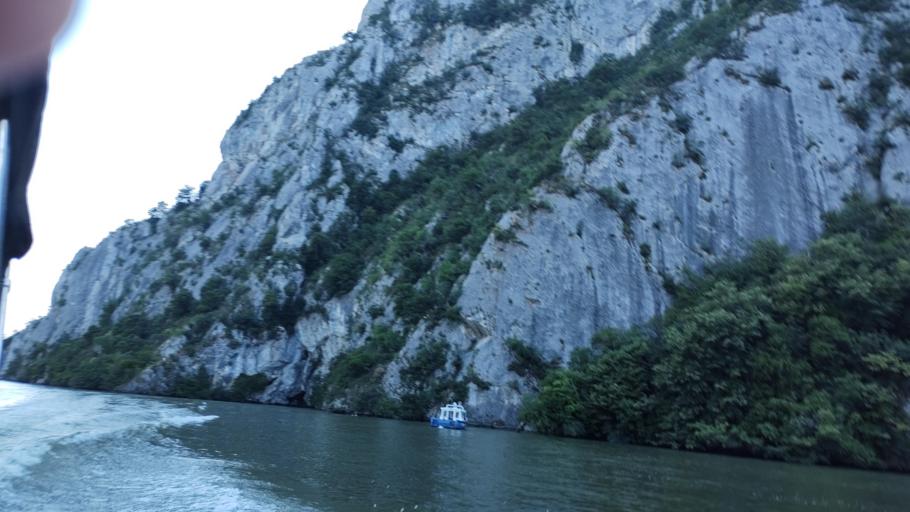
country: RO
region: Mehedinti
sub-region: Comuna Dubova
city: Dubova
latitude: 44.5965
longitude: 22.2630
